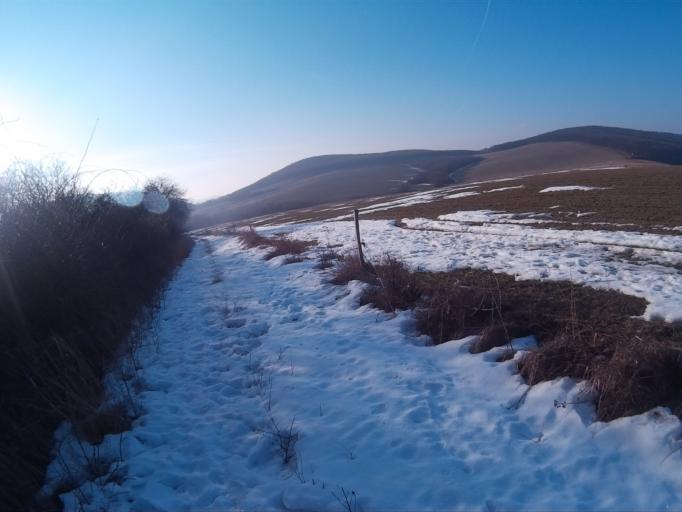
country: HU
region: Nograd
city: Paszto
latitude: 47.9400
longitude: 19.6205
